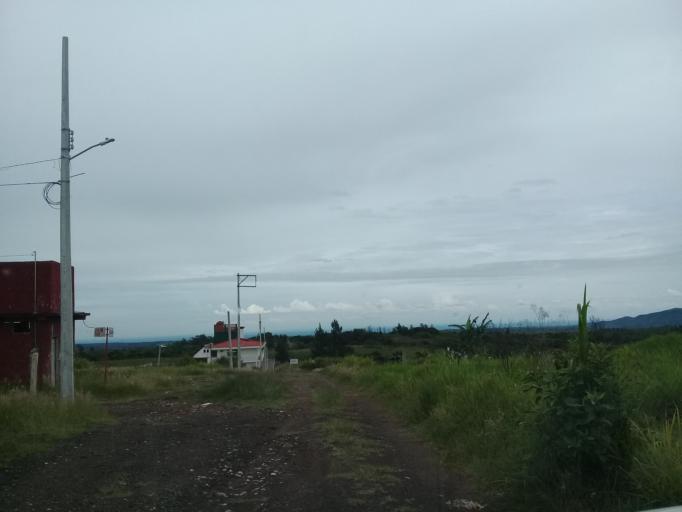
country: MX
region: Veracruz
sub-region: Emiliano Zapata
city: Jacarandas
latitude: 19.4945
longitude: -96.8429
